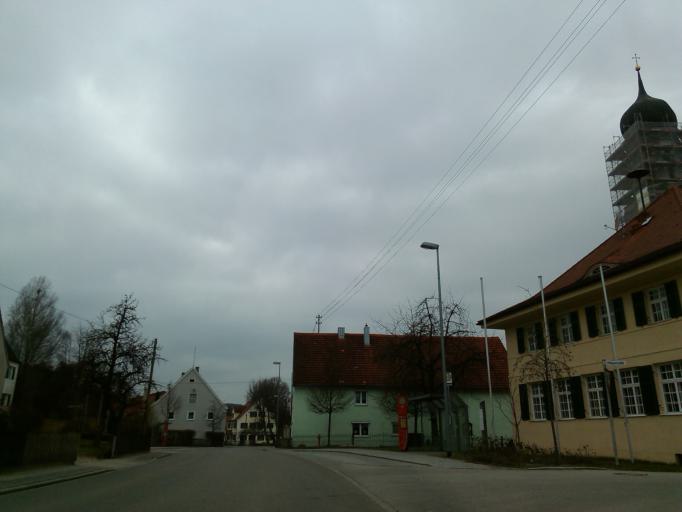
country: DE
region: Bavaria
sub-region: Swabia
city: Ustersbach
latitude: 48.3066
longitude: 10.6135
